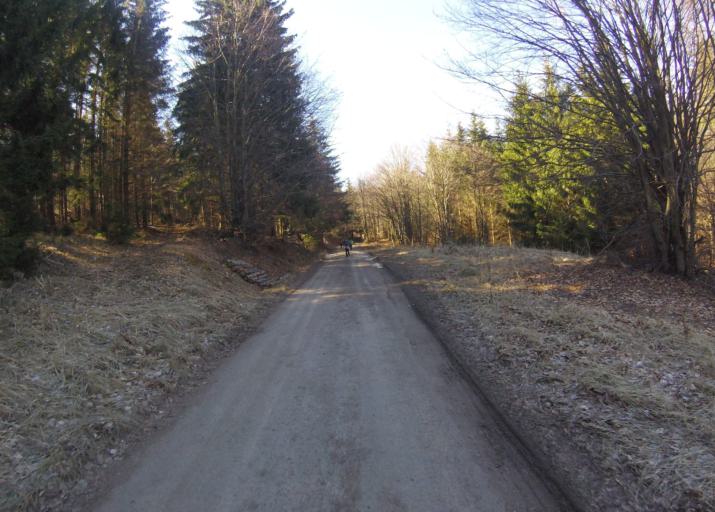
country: HU
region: Heves
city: Szilvasvarad
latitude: 48.0709
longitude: 20.4718
